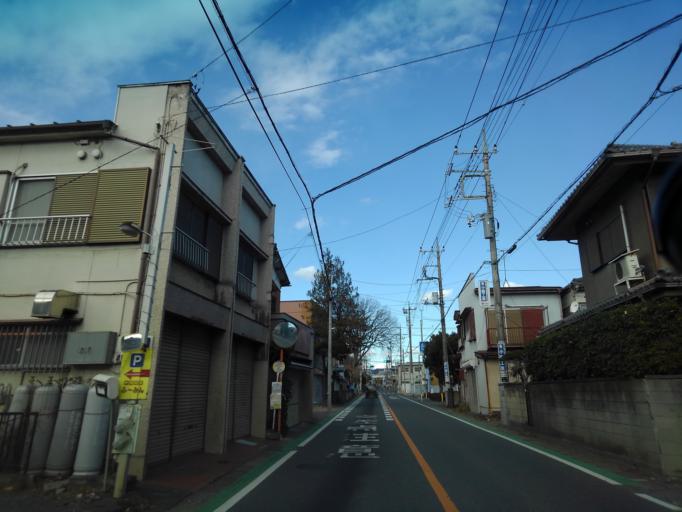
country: JP
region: Saitama
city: Hanno
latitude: 35.8421
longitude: 139.3225
